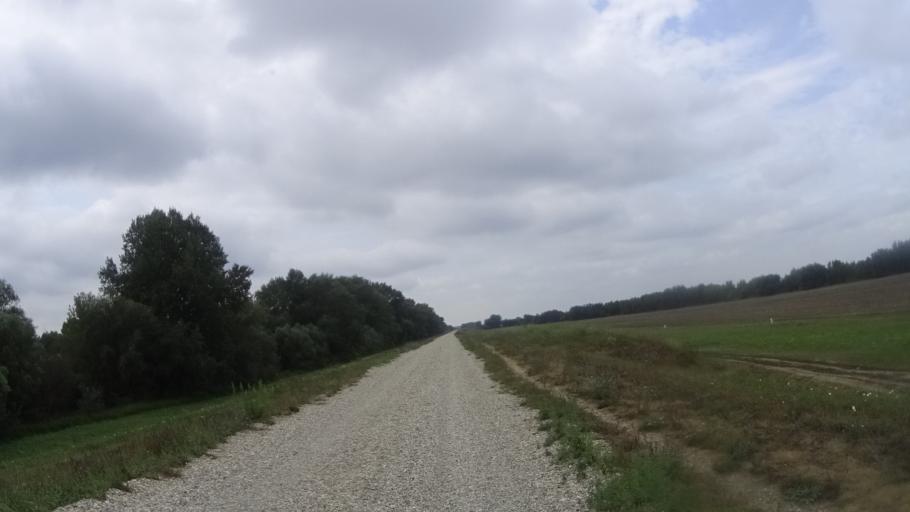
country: HU
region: Komarom-Esztergom
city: Acs
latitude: 47.7554
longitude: 17.9378
